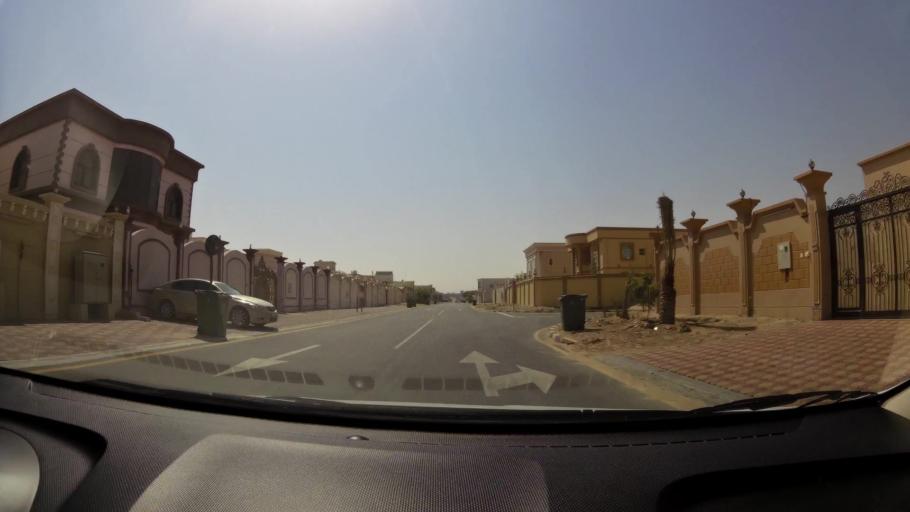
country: AE
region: Ajman
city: Ajman
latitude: 25.4138
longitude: 55.5485
